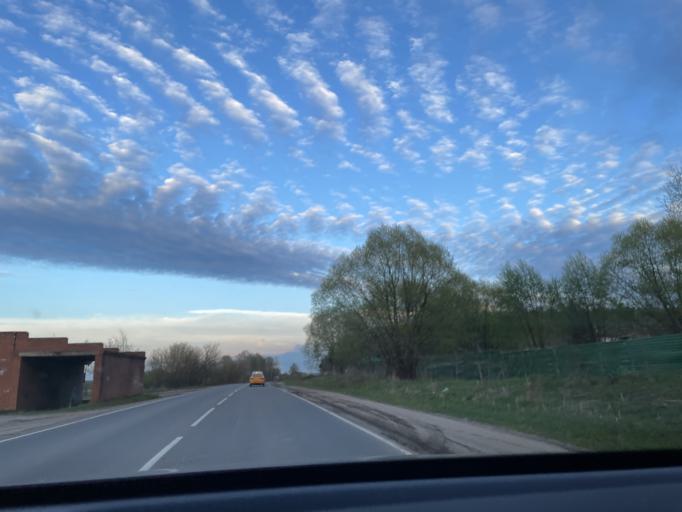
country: RU
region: Moskovskaya
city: Serpukhov
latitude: 54.8728
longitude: 37.4431
